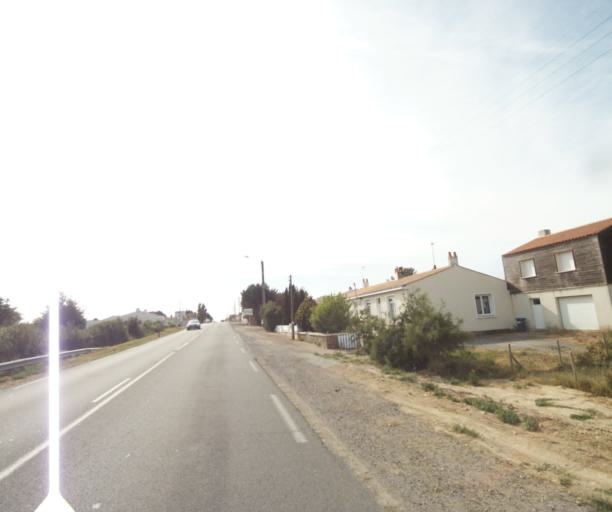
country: FR
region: Pays de la Loire
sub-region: Departement de la Vendee
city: Chateau-d'Olonne
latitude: 46.4838
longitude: -1.7258
